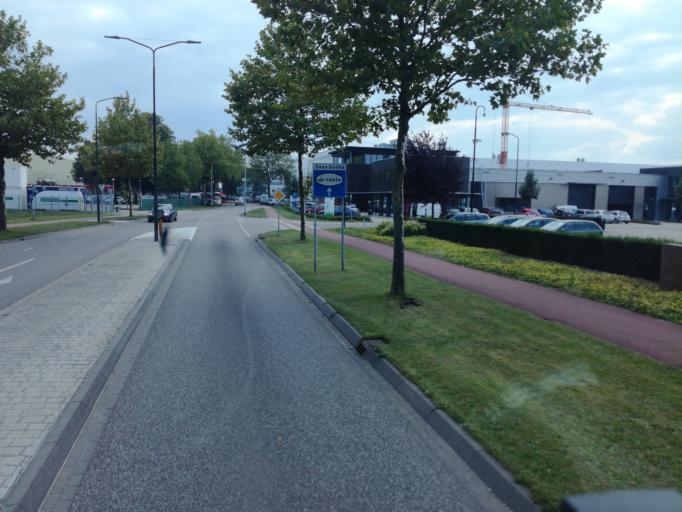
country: NL
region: North Brabant
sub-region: Gemeente Boxmeer
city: Boxmeer
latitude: 51.6430
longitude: 5.9305
